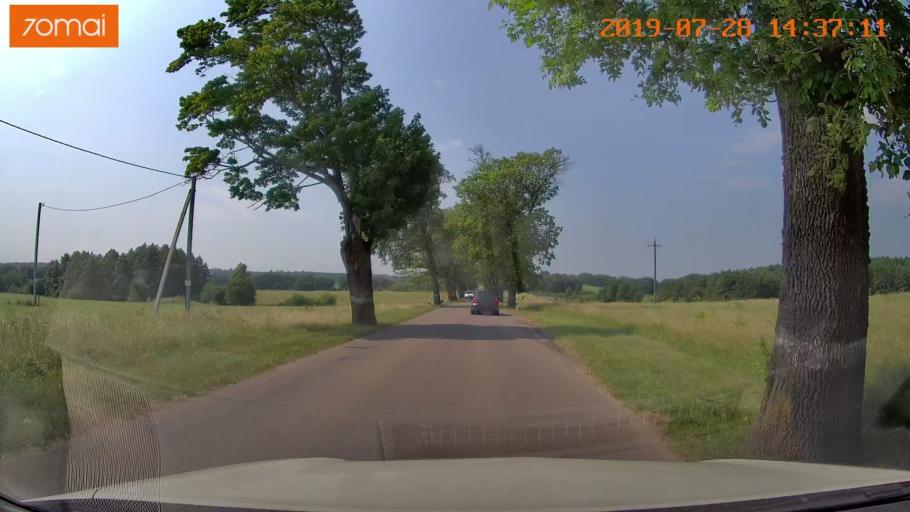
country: RU
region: Kaliningrad
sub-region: Gorod Kaliningrad
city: Yantarnyy
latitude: 54.8403
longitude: 20.0016
